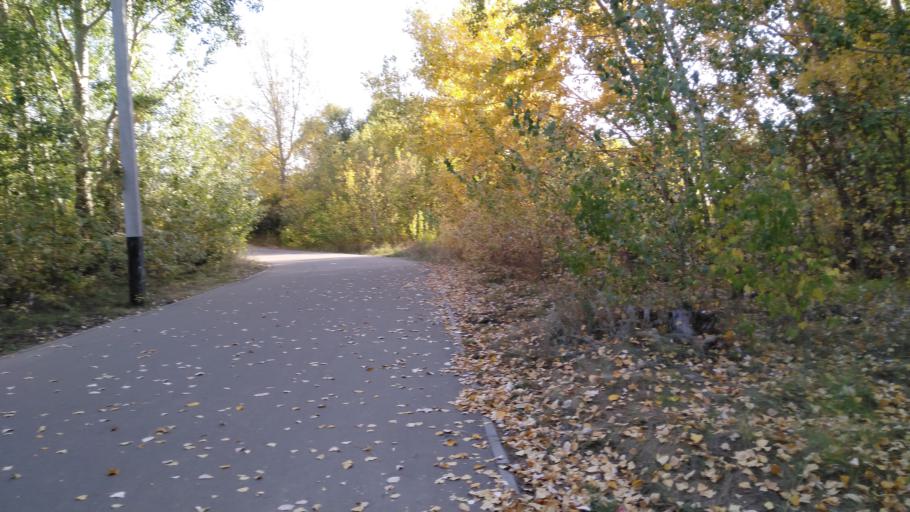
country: KZ
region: Pavlodar
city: Pavlodar
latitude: 52.2630
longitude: 76.9320
